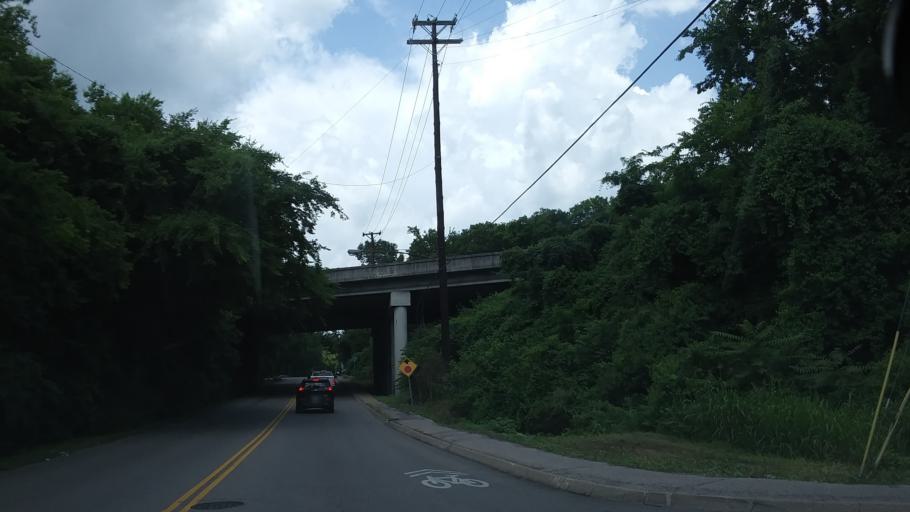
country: US
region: Tennessee
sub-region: Davidson County
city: Belle Meade
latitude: 36.1415
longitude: -86.8843
